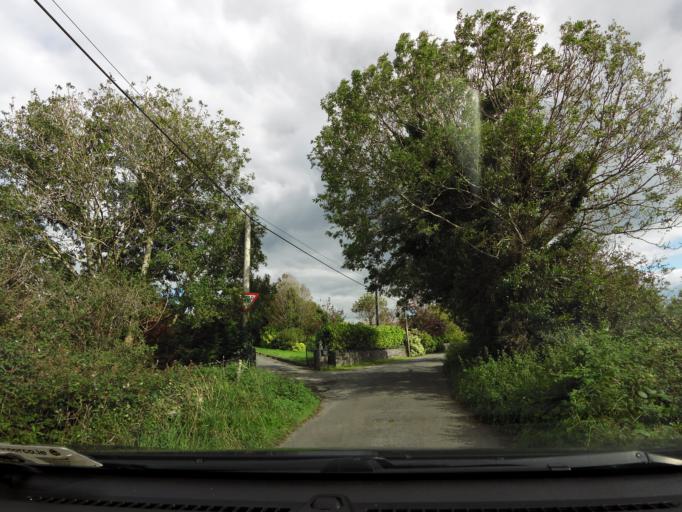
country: IE
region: Connaught
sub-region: County Galway
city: Moycullen
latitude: 53.3206
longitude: -9.1436
